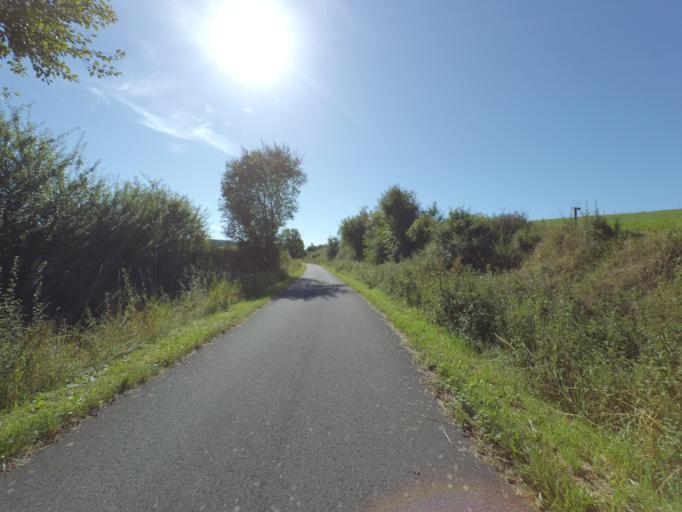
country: DE
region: Rheinland-Pfalz
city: Udler
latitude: 50.1410
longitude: 6.8810
